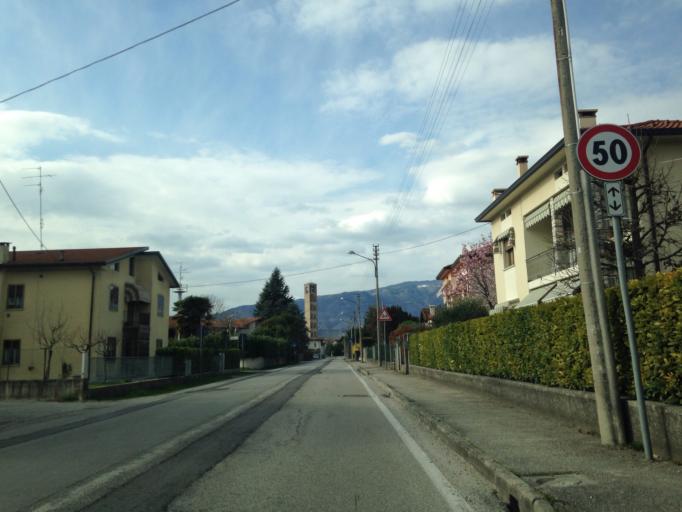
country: IT
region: Friuli Venezia Giulia
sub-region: Provincia di Pordenone
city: Sacile
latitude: 45.9466
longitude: 12.5089
